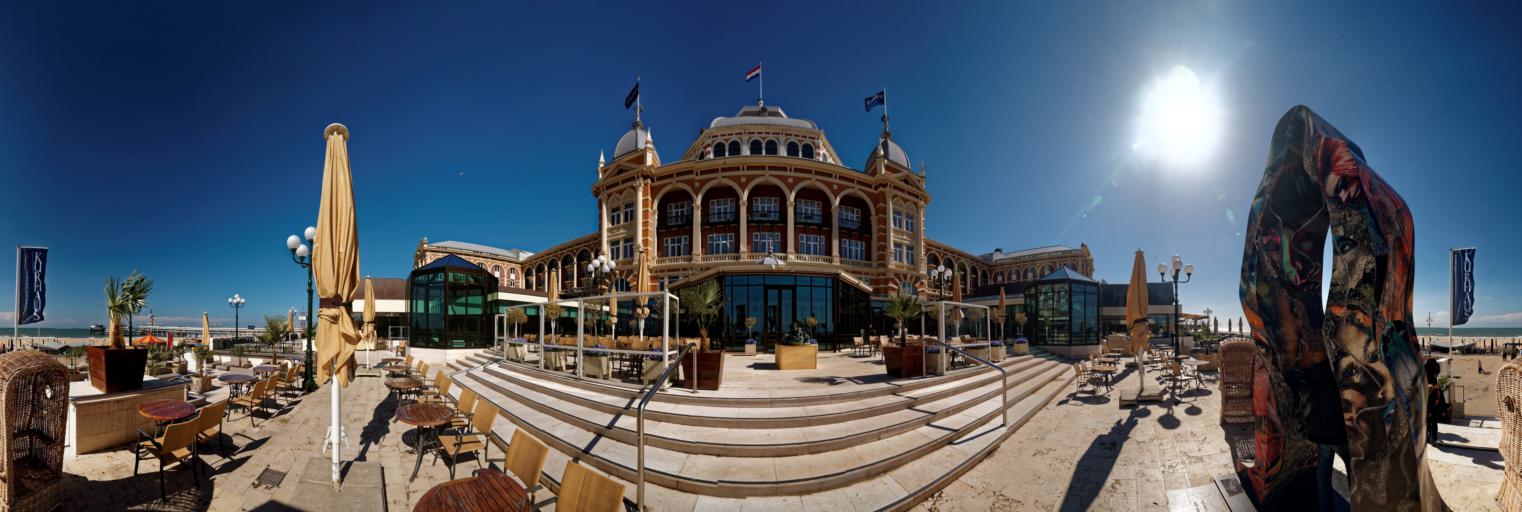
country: NL
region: South Holland
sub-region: Gemeente Den Haag
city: Scheveningen
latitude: 52.1134
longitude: 4.2814
